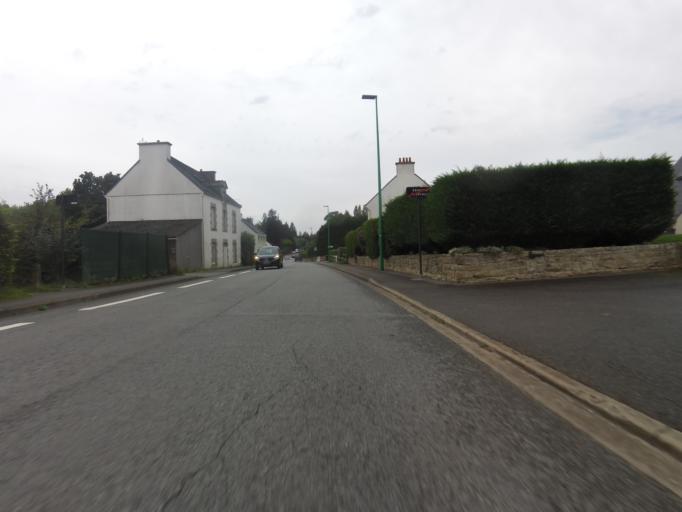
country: FR
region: Brittany
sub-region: Departement du Morbihan
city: Saint-Ave
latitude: 47.6967
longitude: -2.7498
